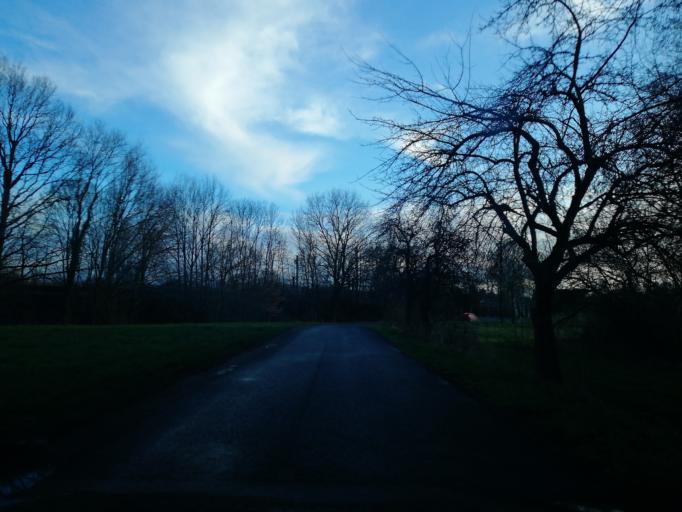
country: DE
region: Brandenburg
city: Calau
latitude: 51.7297
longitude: 13.9570
